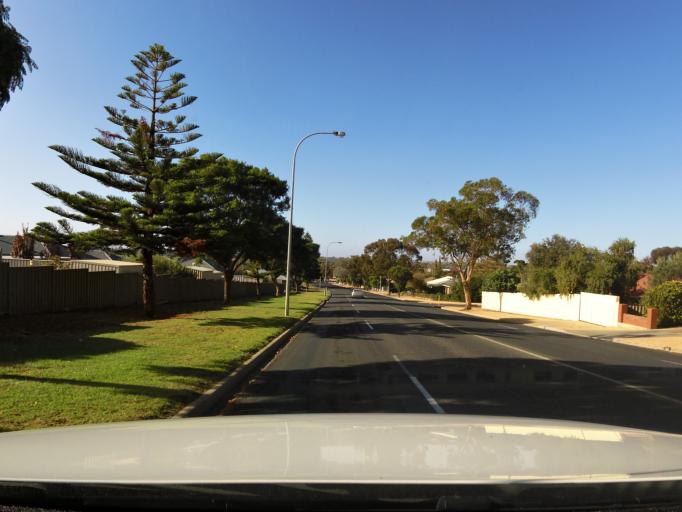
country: AU
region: South Australia
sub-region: Berri and Barmera
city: Berri
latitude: -34.2738
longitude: 140.6078
